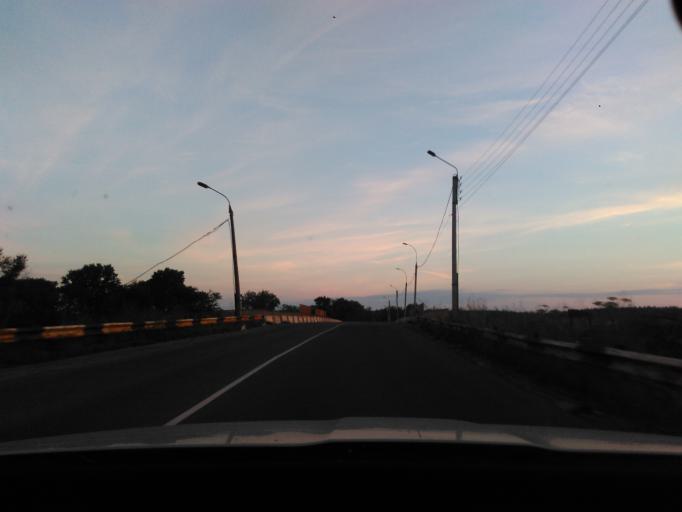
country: RU
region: Moskovskaya
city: Klin
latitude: 56.2691
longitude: 36.7621
